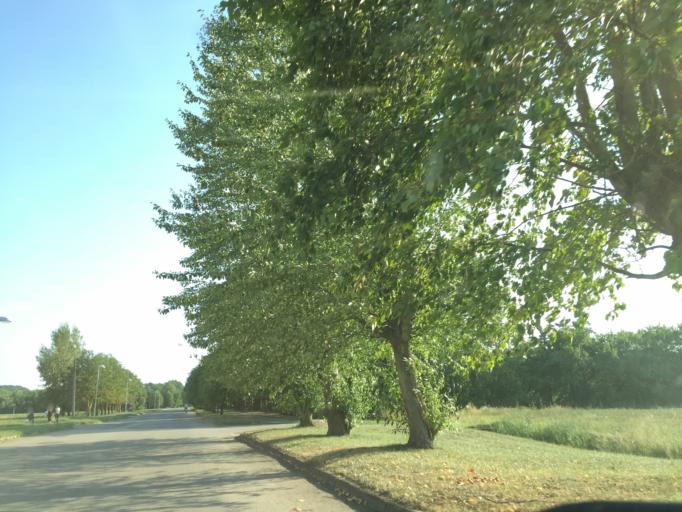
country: LT
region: Siauliu apskritis
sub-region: Joniskis
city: Joniskis
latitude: 56.4174
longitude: 23.6978
